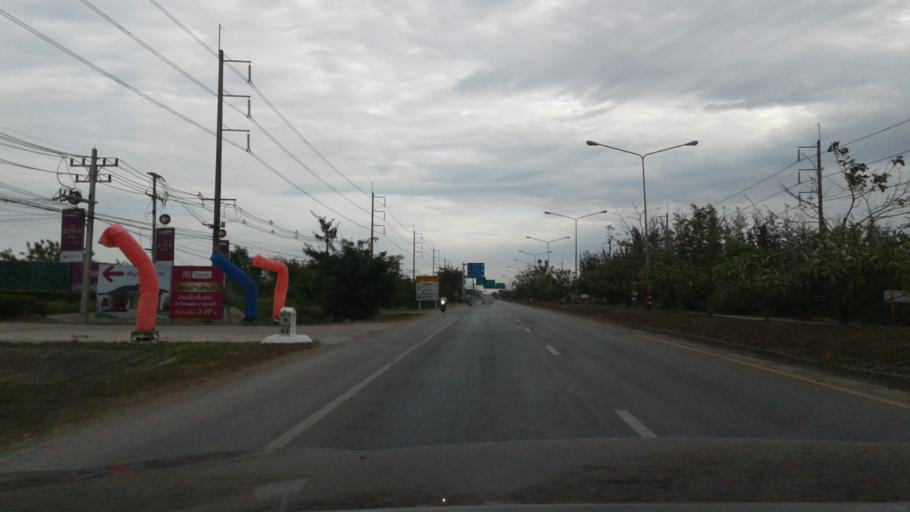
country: TH
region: Changwat Udon Thani
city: Udon Thani
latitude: 17.3691
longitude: 102.7167
